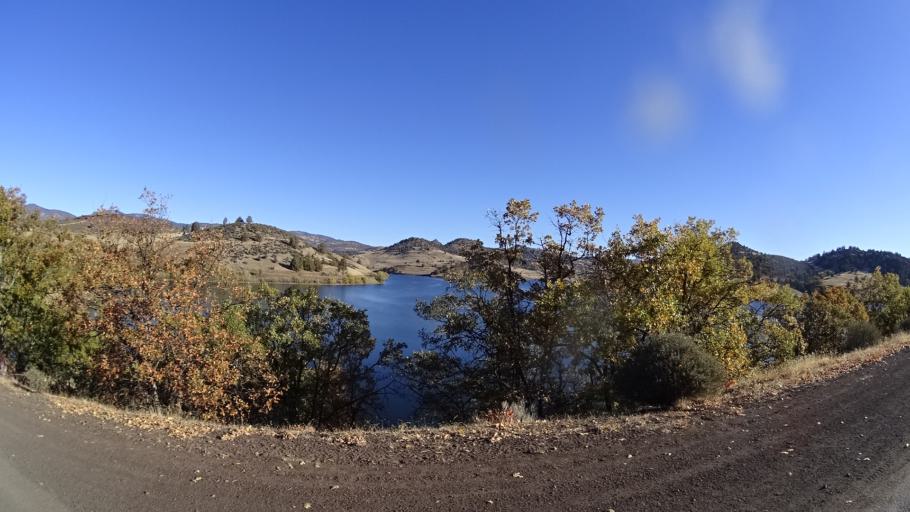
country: US
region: California
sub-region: Siskiyou County
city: Montague
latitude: 41.9523
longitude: -122.4380
